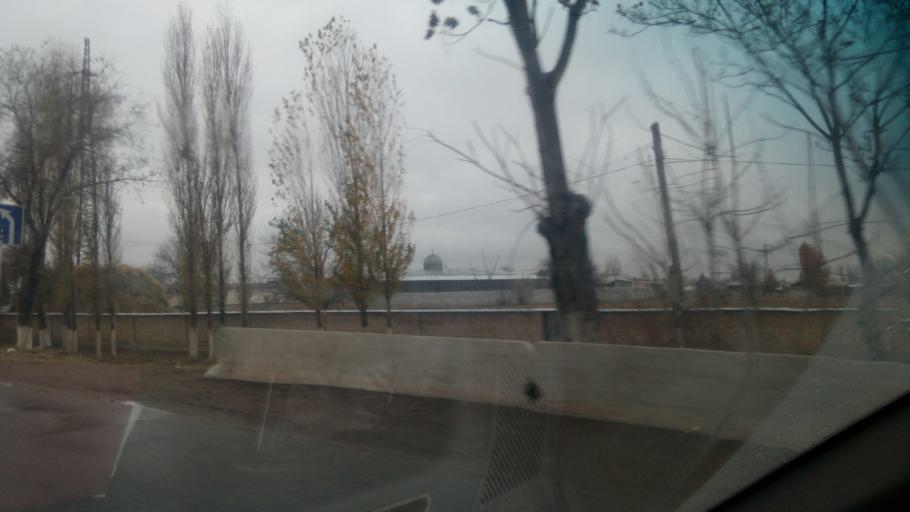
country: UZ
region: Toshkent
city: Urtaowul
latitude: 41.2235
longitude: 69.1406
